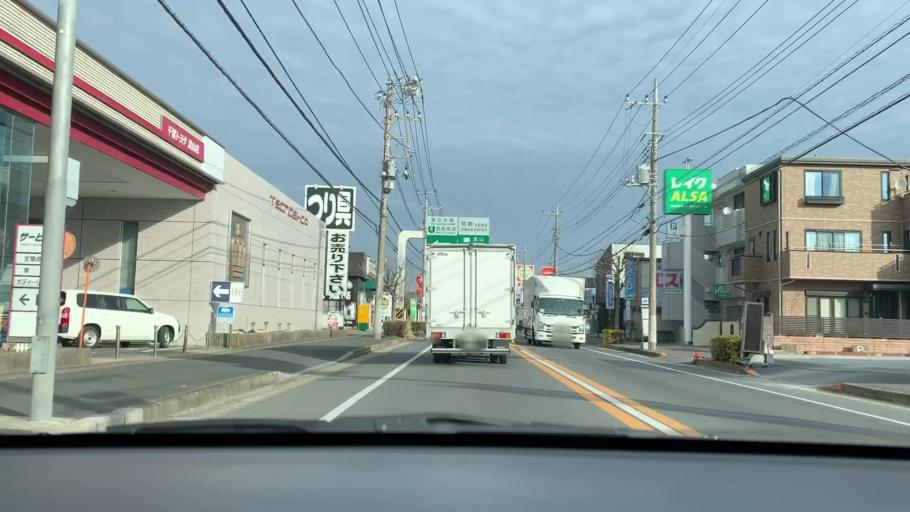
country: JP
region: Chiba
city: Nagareyama
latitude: 35.8403
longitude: 139.8970
